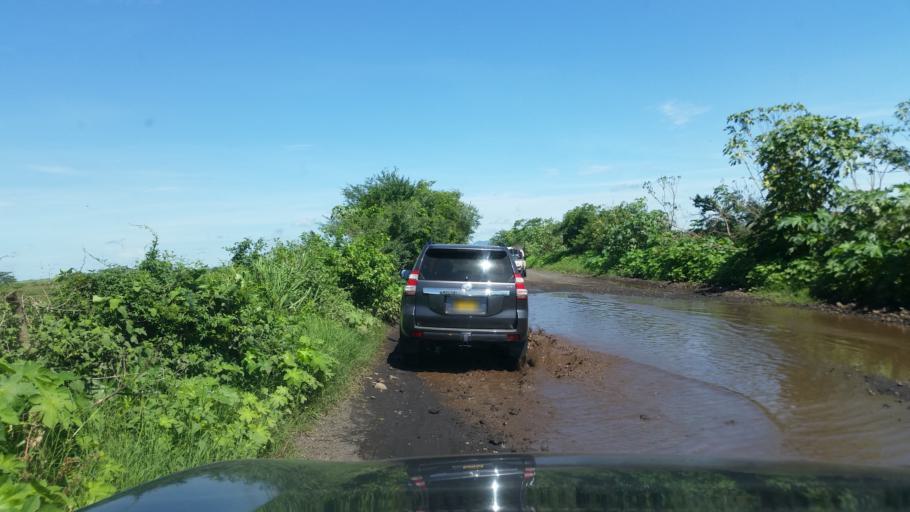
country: NI
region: Chinandega
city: Puerto Morazan
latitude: 12.7730
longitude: -87.0976
